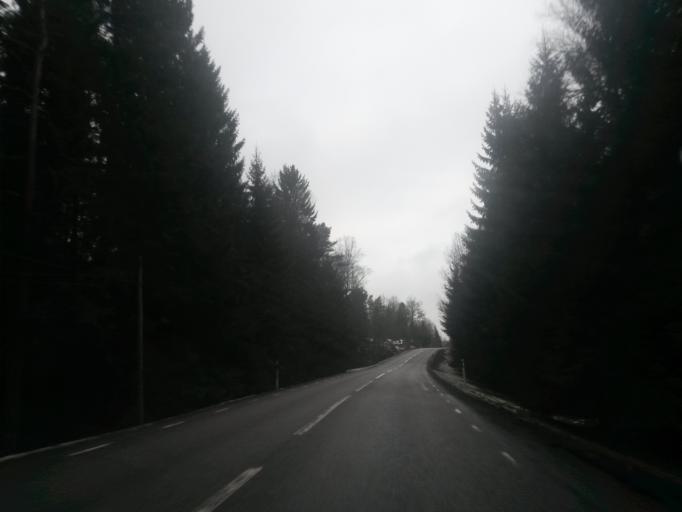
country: SE
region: Vaestra Goetaland
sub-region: Alingsas Kommun
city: Sollebrunn
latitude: 58.1309
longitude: 12.4902
